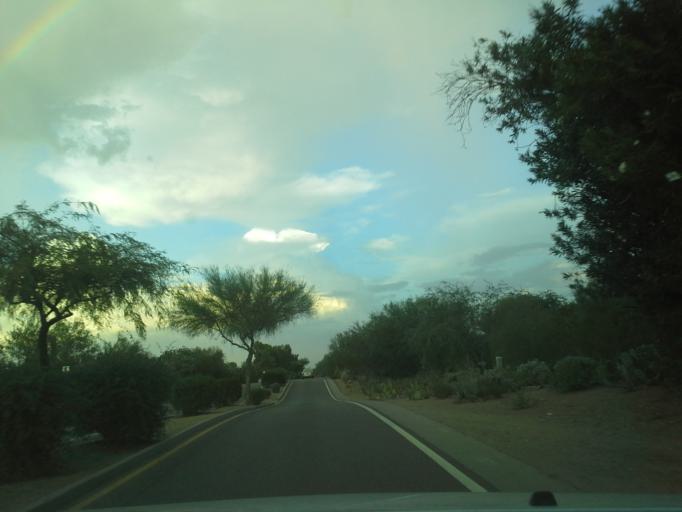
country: US
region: Arizona
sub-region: Maricopa County
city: Paradise Valley
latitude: 33.5238
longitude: -111.9574
